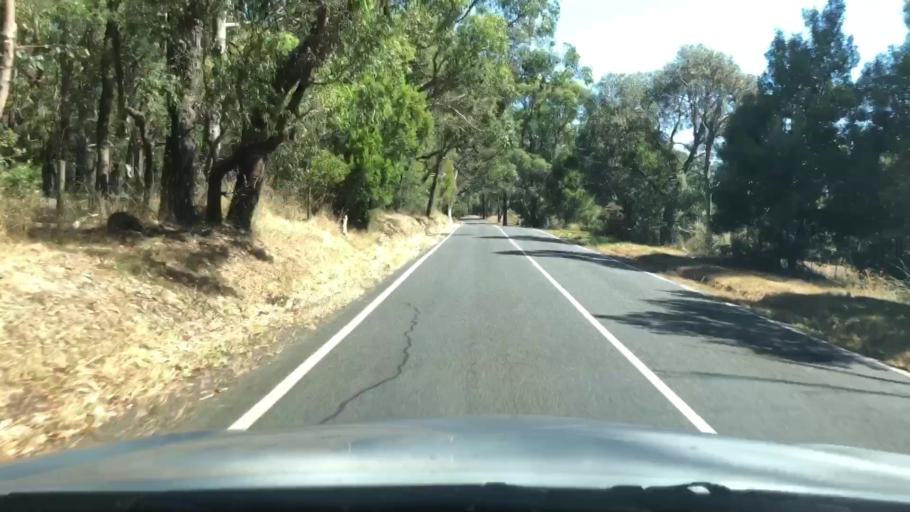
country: AU
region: Victoria
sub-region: Yarra Ranges
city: Macclesfield
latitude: -37.8308
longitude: 145.4879
